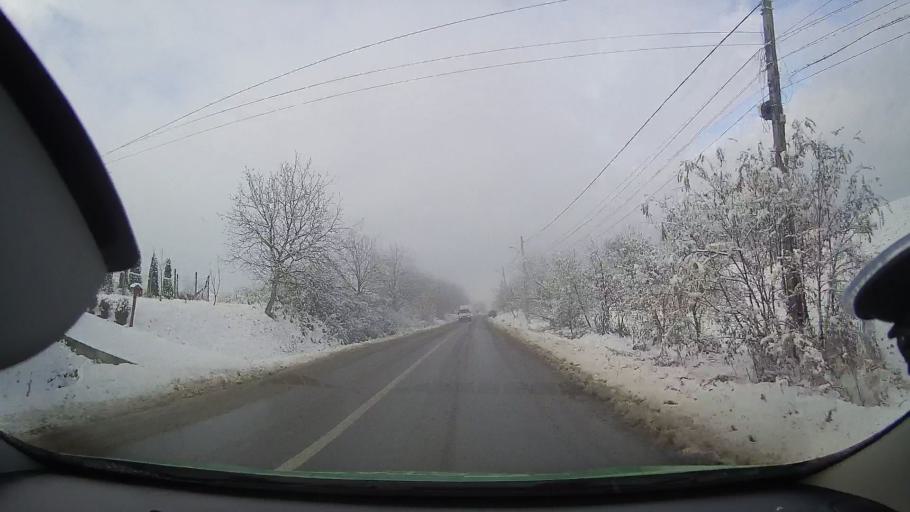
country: RO
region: Mures
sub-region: Comuna Atintis
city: Atintis
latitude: 46.4365
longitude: 24.0947
